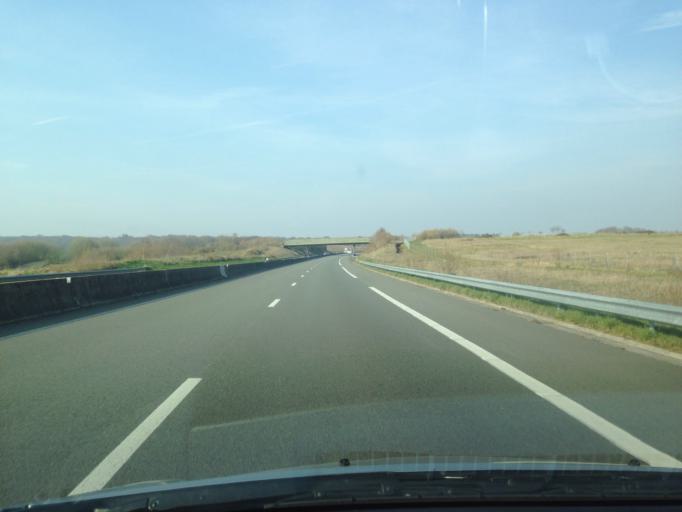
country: FR
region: Nord-Pas-de-Calais
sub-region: Departement du Pas-de-Calais
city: Saint-Josse
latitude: 50.4472
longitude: 1.6939
